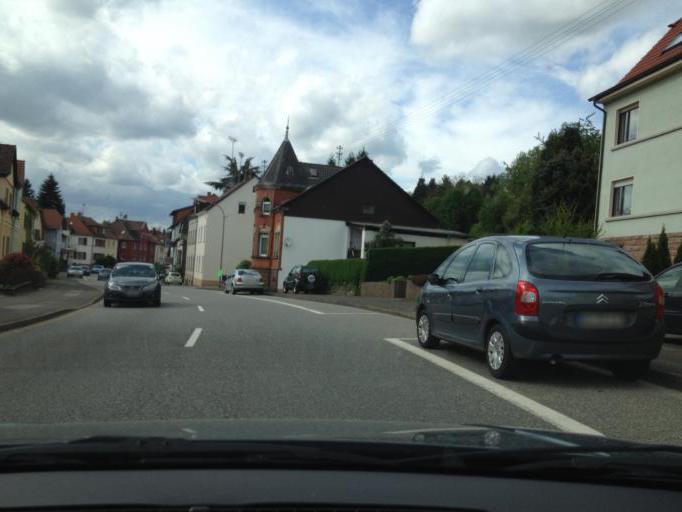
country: DE
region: Saarland
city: Ottweiler
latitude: 49.3970
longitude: 7.1706
